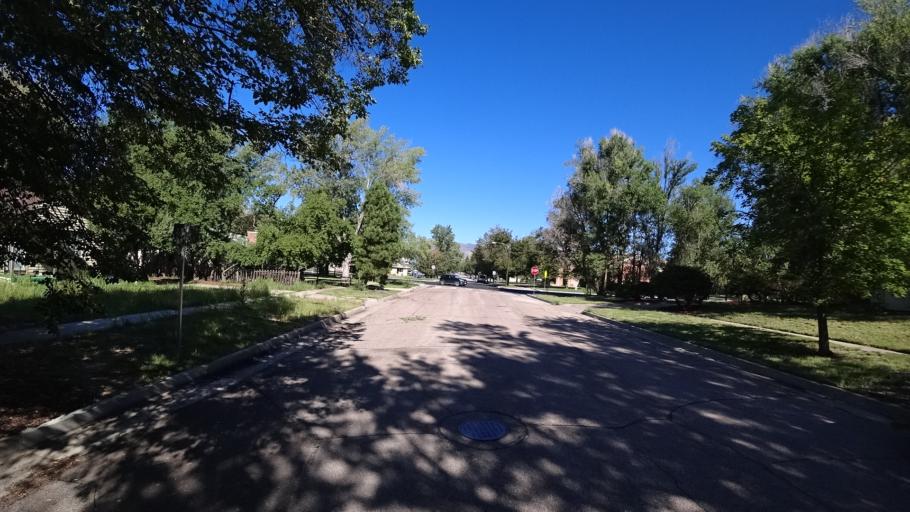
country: US
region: Colorado
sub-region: El Paso County
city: Colorado Springs
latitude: 38.8648
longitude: -104.8036
